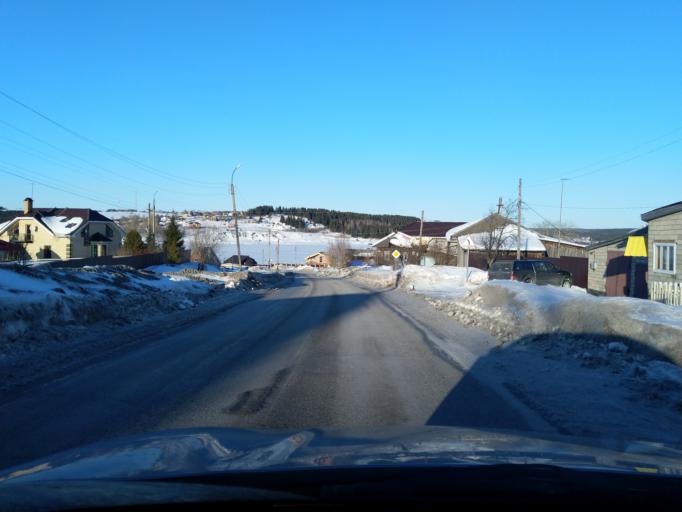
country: RU
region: Perm
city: Polazna
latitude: 58.2982
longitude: 56.4177
